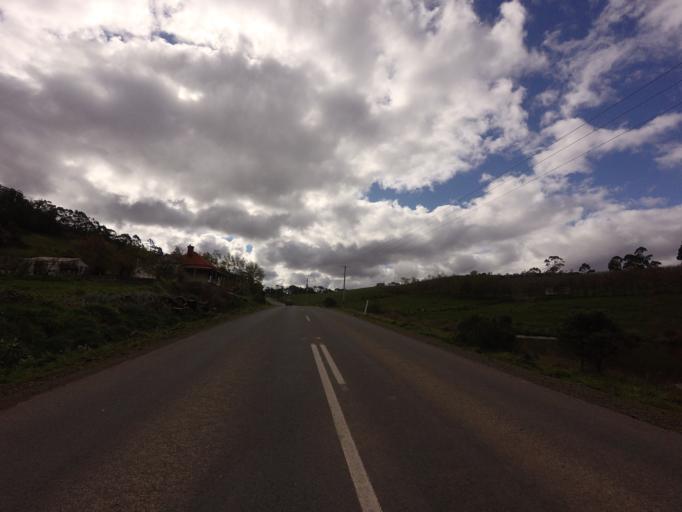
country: AU
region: Tasmania
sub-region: Huon Valley
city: Geeveston
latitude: -43.1857
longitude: 146.9561
